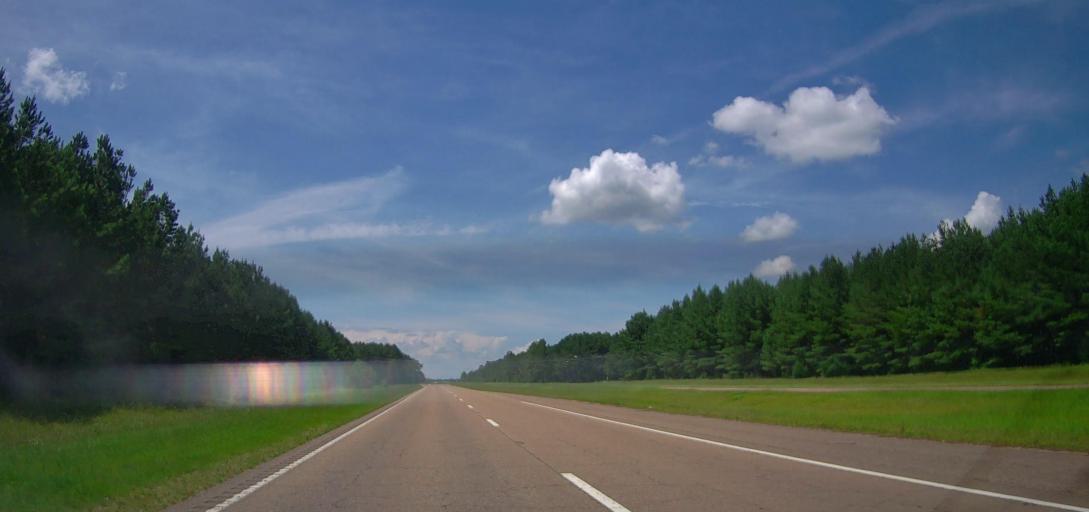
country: US
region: Mississippi
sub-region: Monroe County
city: Aberdeen
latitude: 33.8232
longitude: -88.5839
